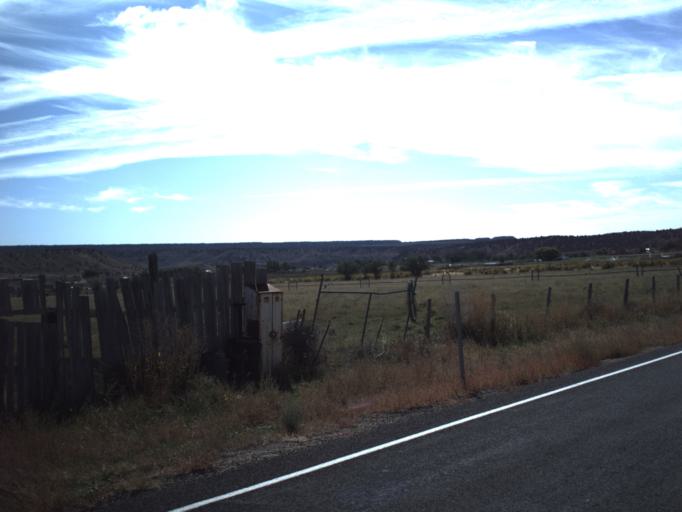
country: US
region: Utah
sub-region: Garfield County
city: Panguitch
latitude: 37.6327
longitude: -112.0819
